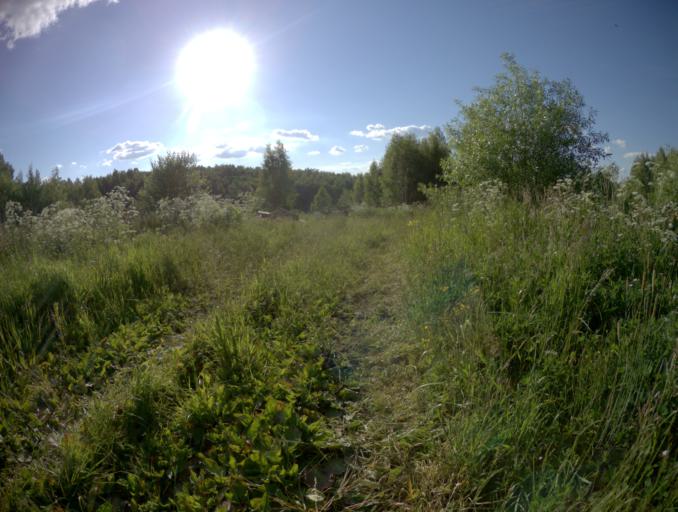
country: RU
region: Vladimir
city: Stavrovo
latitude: 56.2459
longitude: 40.0854
